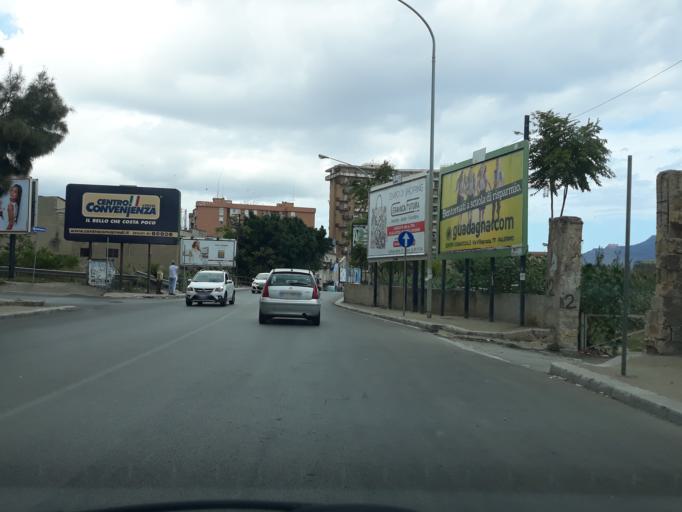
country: IT
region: Sicily
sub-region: Palermo
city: Ciaculli
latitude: 38.1093
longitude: 13.3799
